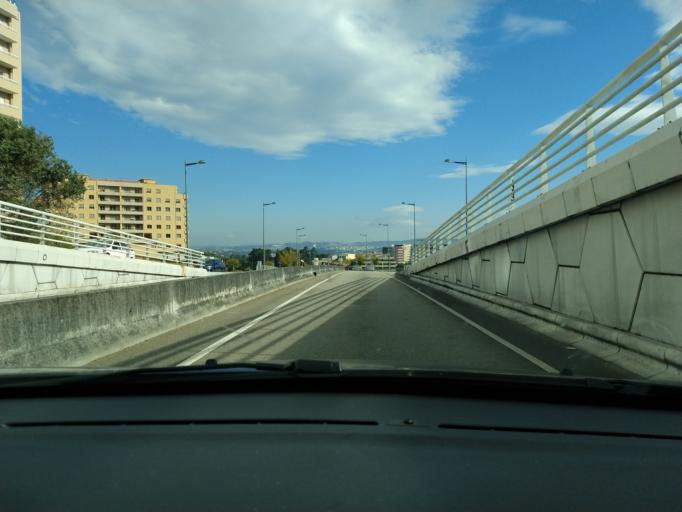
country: PT
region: Porto
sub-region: Vila Nova de Gaia
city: Vilar de Andorinho
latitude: 41.1210
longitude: -8.6000
